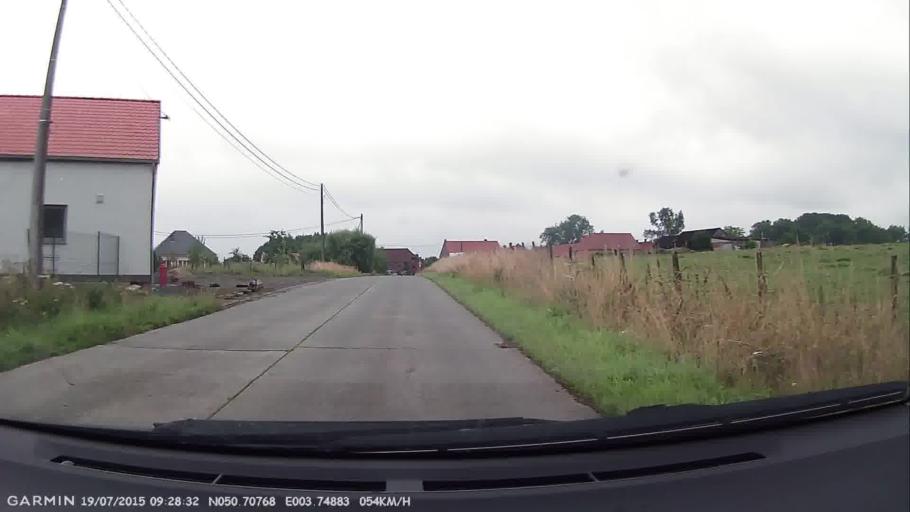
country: BE
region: Wallonia
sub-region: Province du Hainaut
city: Flobecq
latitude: 50.7075
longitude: 3.7489
